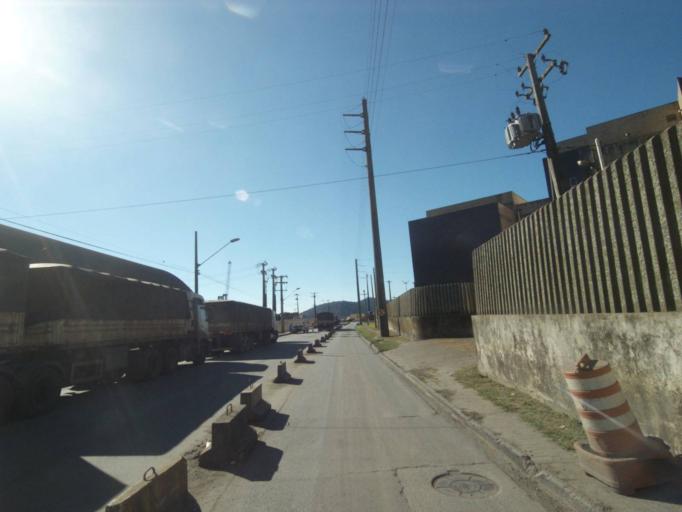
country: BR
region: Parana
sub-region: Paranagua
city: Paranagua
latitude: -25.5074
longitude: -48.5070
